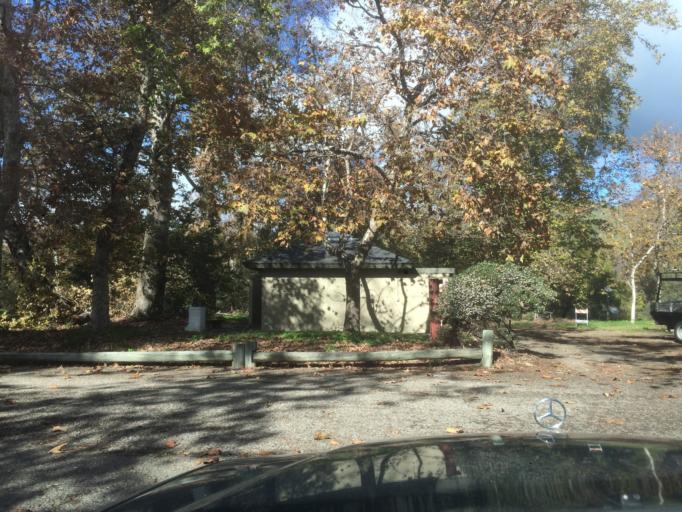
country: US
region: California
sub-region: San Luis Obispo County
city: Arroyo Grande
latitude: 35.1790
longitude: -120.5158
